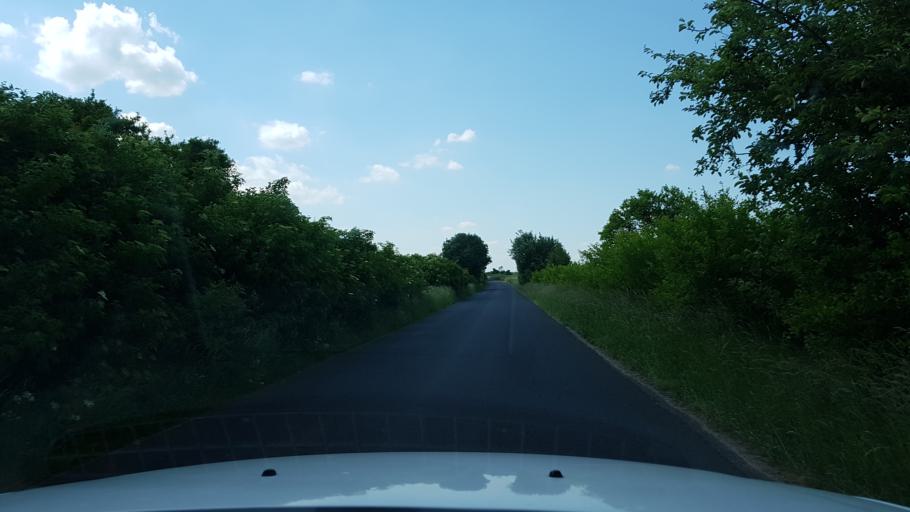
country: PL
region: West Pomeranian Voivodeship
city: Trzcinsko Zdroj
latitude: 52.9926
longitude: 14.5861
